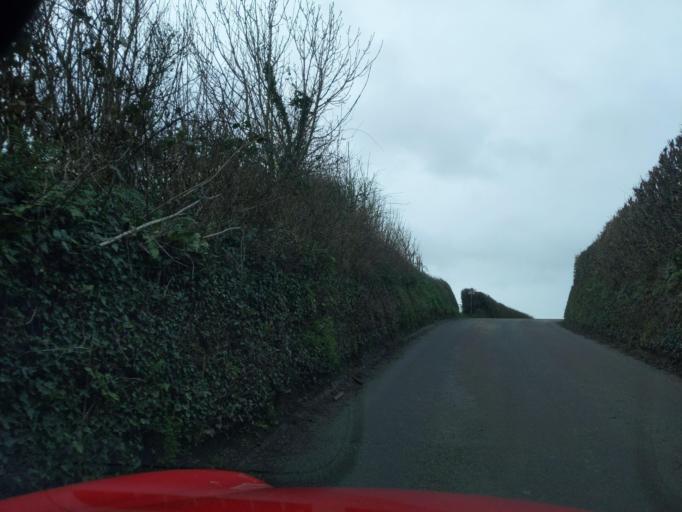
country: GB
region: England
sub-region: Devon
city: Modbury
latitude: 50.3385
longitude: -3.8671
